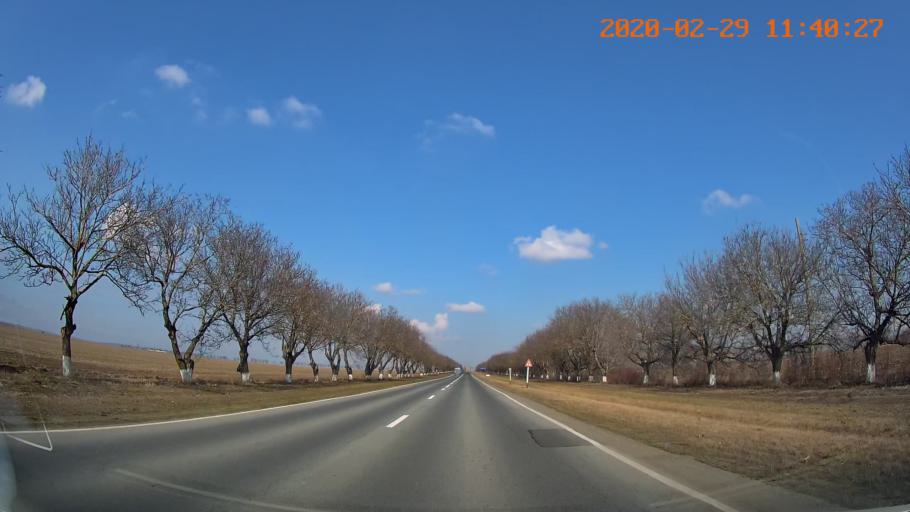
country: MD
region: Rezina
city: Saharna
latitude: 47.6564
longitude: 29.0202
